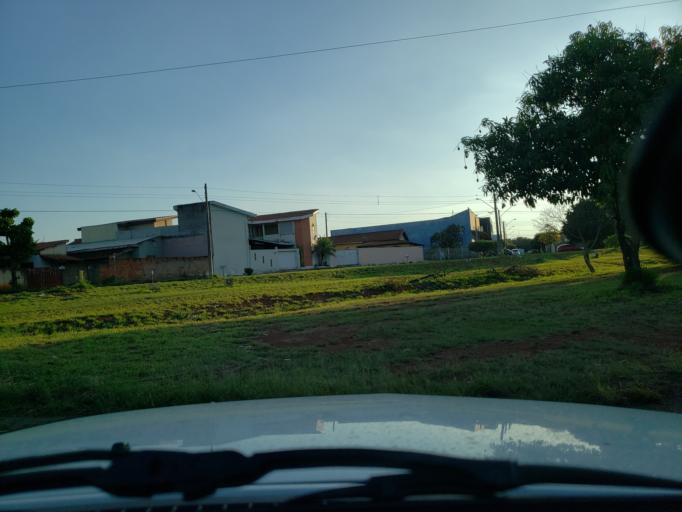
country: BR
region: Sao Paulo
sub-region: Moji-Guacu
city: Mogi-Gaucu
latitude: -22.3420
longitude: -46.9391
